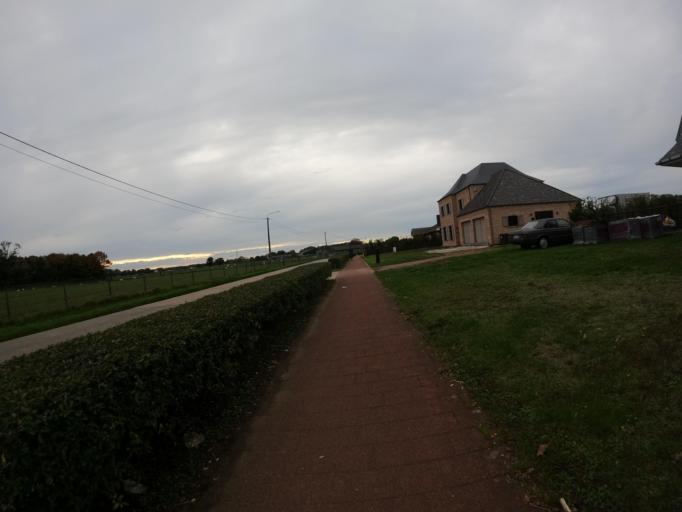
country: BE
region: Flanders
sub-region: Provincie Antwerpen
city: Herenthout
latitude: 51.1274
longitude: 4.7919
